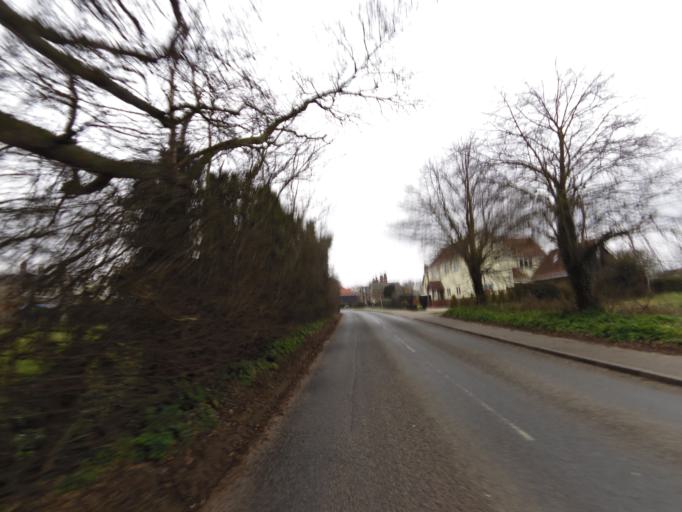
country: GB
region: England
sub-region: Suffolk
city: Wickham Market
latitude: 52.1513
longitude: 1.3966
